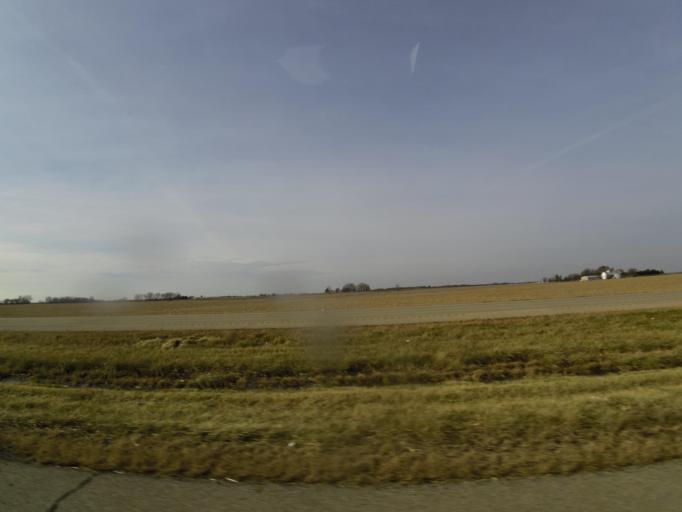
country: US
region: Illinois
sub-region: McLean County
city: Bloomington
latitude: 40.4038
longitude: -88.9895
